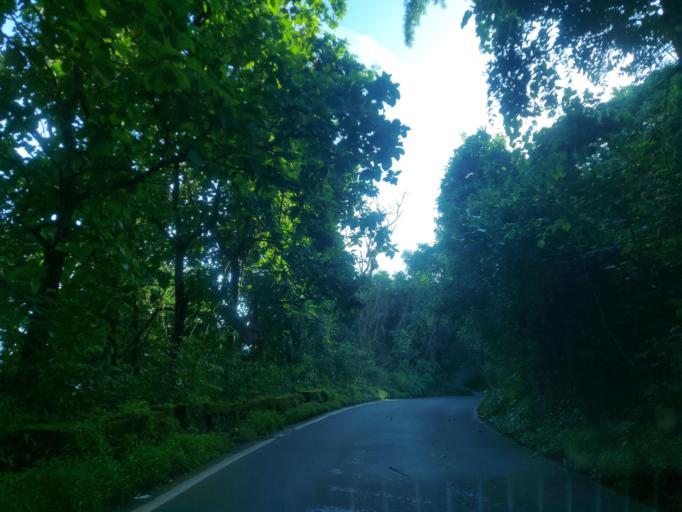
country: IN
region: Maharashtra
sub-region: Sindhudurg
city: Savantvadi
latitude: 15.9363
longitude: 73.9440
